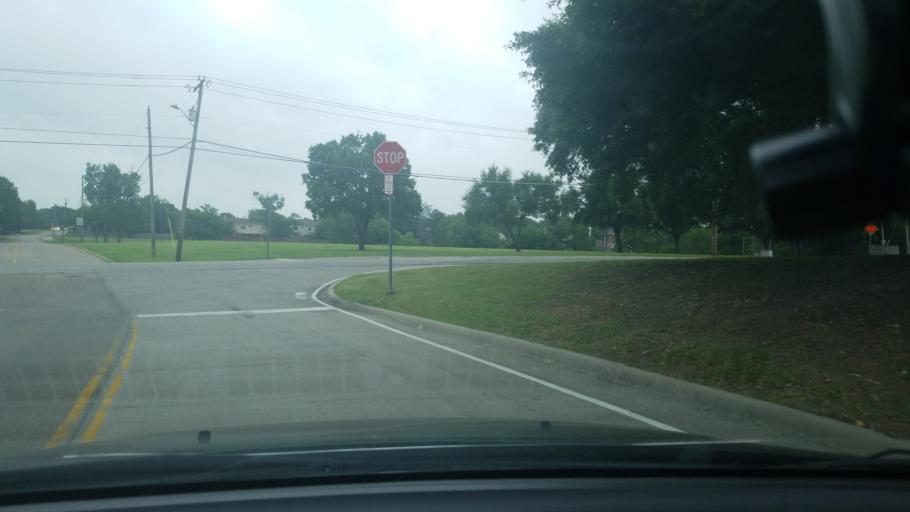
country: US
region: Texas
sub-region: Dallas County
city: Mesquite
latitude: 32.7918
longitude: -96.6492
